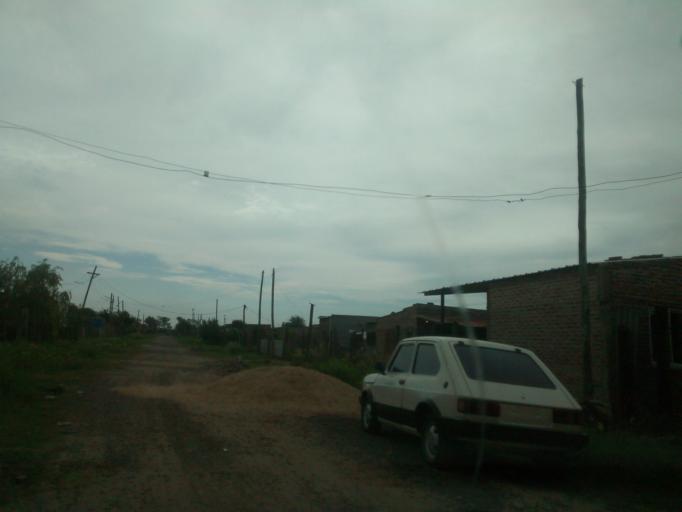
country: AR
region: Chaco
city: Fontana
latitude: -27.4660
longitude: -59.0333
